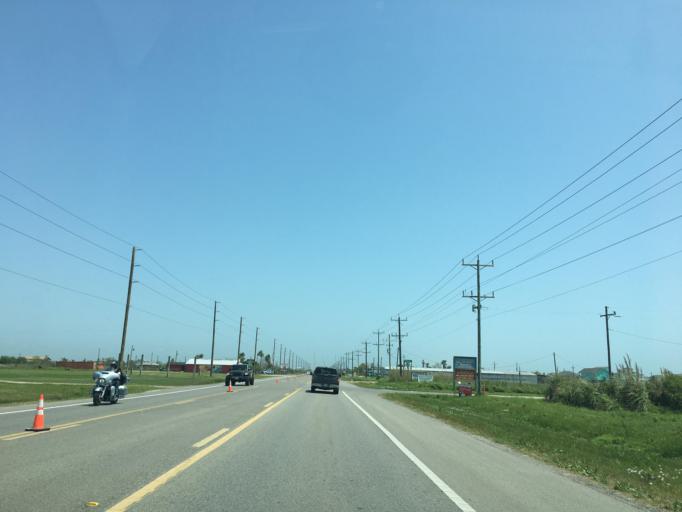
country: US
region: Texas
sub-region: Galveston County
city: Bolivar Peninsula
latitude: 29.4454
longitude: -94.6609
